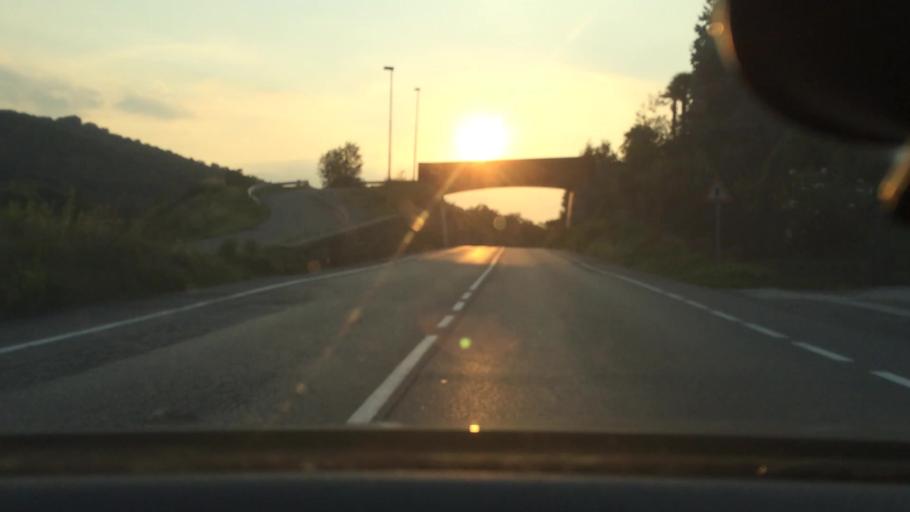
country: IT
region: Lombardy
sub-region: Provincia di Lecco
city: Perego
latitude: 45.7399
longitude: 9.3577
